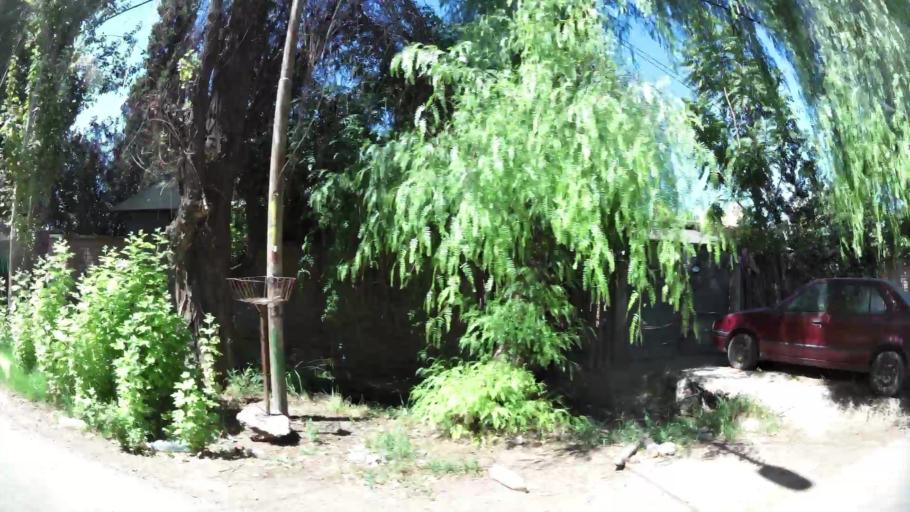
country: AR
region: Mendoza
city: Las Heras
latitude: -32.8673
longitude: -68.7992
